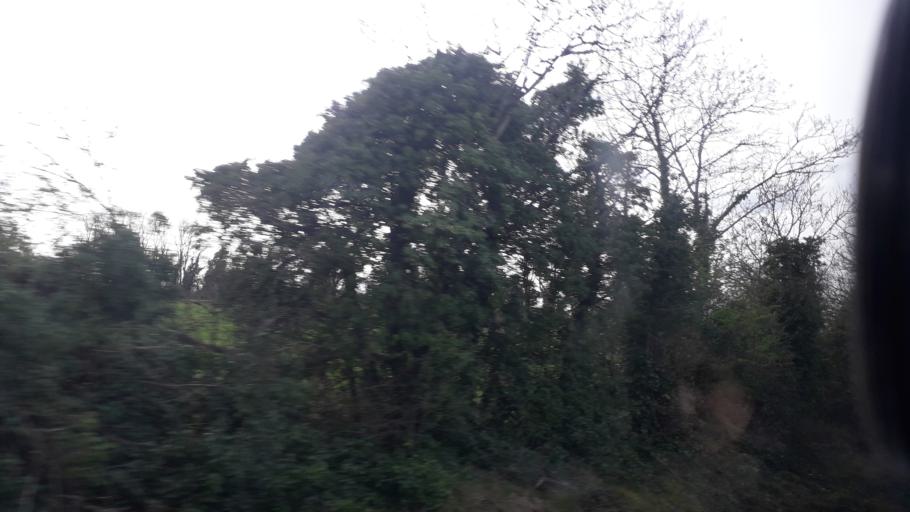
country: IE
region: Leinster
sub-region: Kildare
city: Kilcock
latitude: 53.4130
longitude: -6.6925
